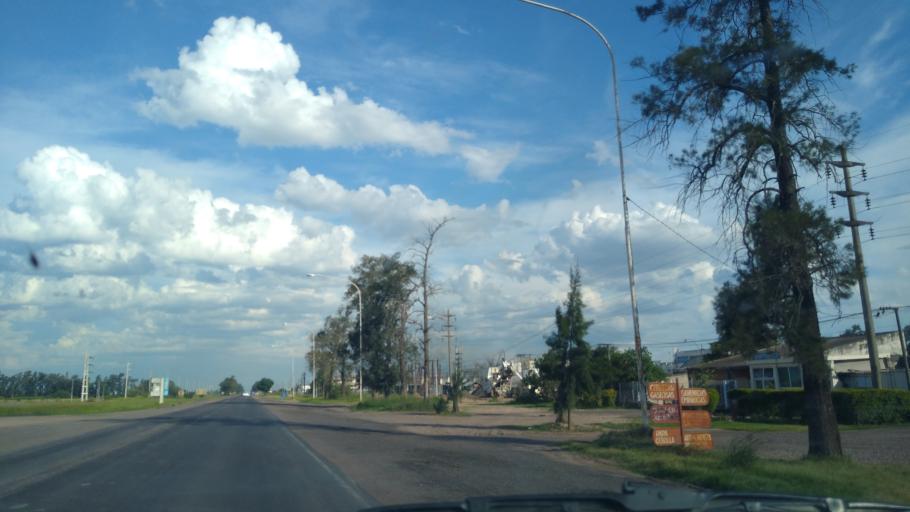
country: AR
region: Chaco
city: Presidencia Roque Saenz Pena
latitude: -26.8140
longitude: -60.4142
